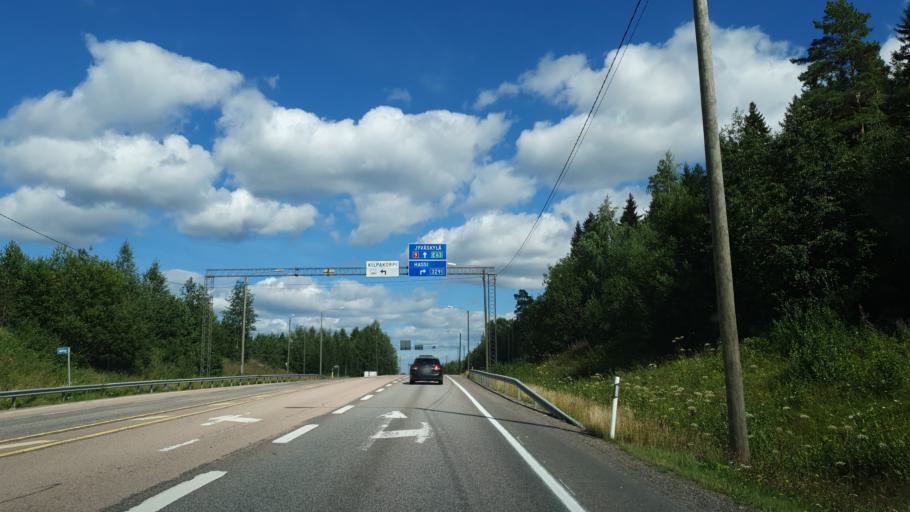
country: FI
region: Central Finland
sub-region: Jaemsae
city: Jaemsae
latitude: 61.8456
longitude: 25.1461
